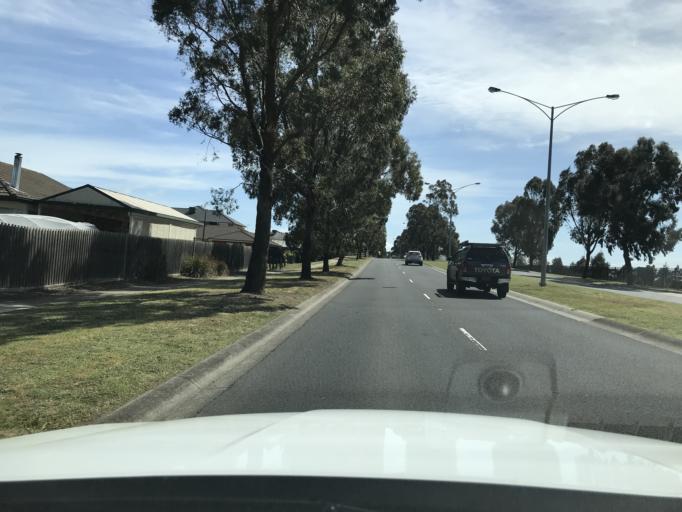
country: AU
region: Victoria
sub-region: Hume
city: Roxburgh Park
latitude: -37.6237
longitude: 144.9328
